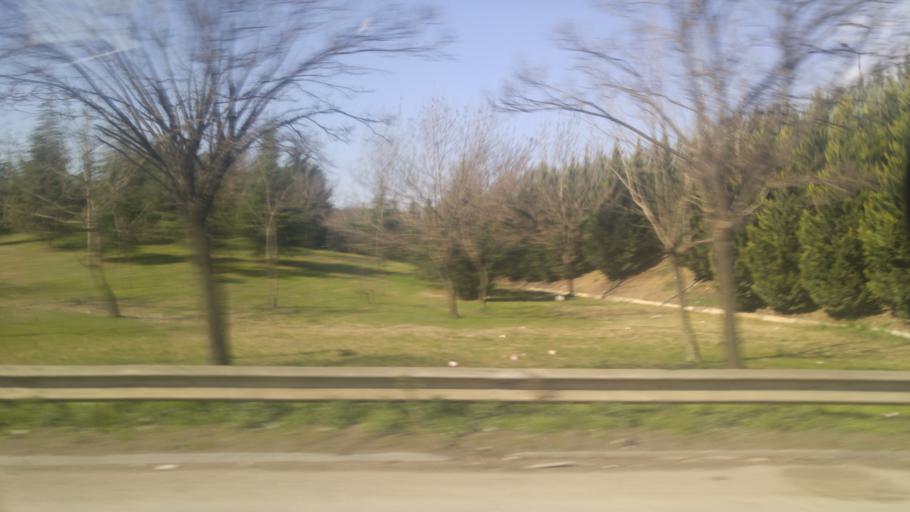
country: TR
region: Kocaeli
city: Darica
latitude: 40.8173
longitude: 29.3650
